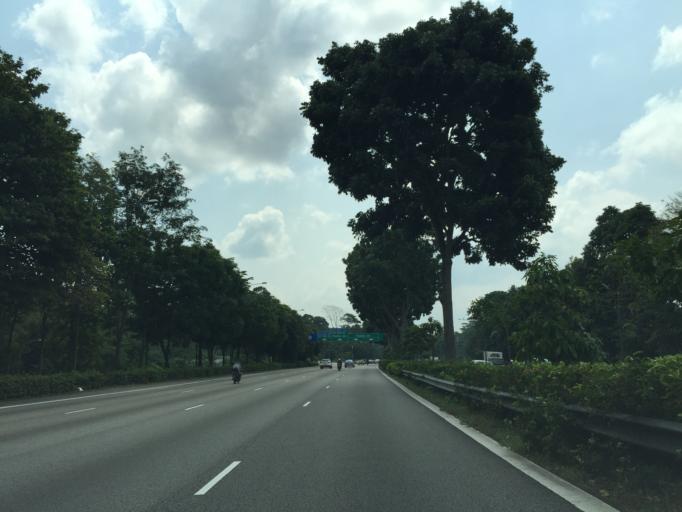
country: MY
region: Johor
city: Johor Bahru
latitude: 1.4077
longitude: 103.7721
